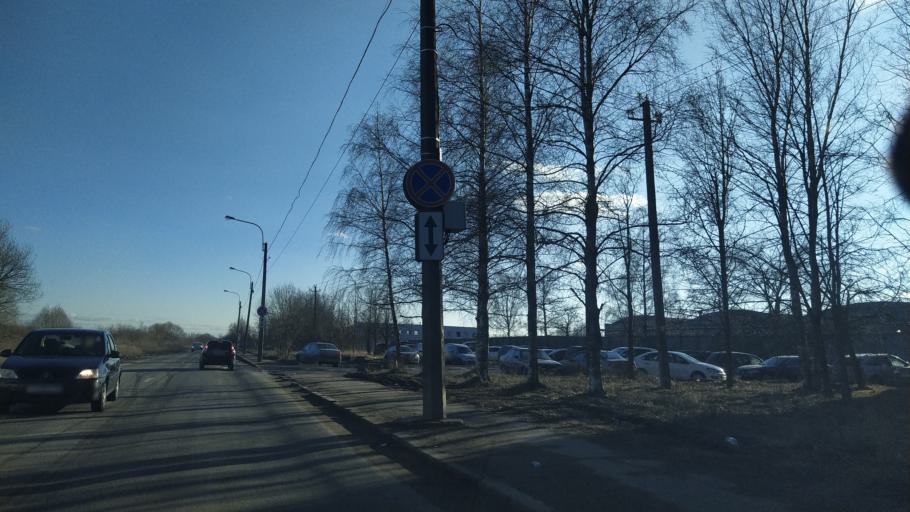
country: RU
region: St.-Petersburg
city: Pushkin
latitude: 59.6968
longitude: 30.3953
